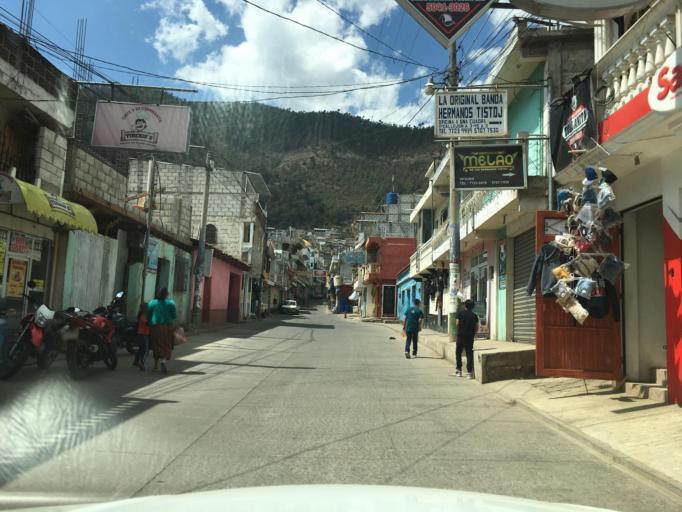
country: GT
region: Totonicapan
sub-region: Municipio de San Andres Xecul
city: San Andres Xecul
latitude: 14.9049
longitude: -91.4808
